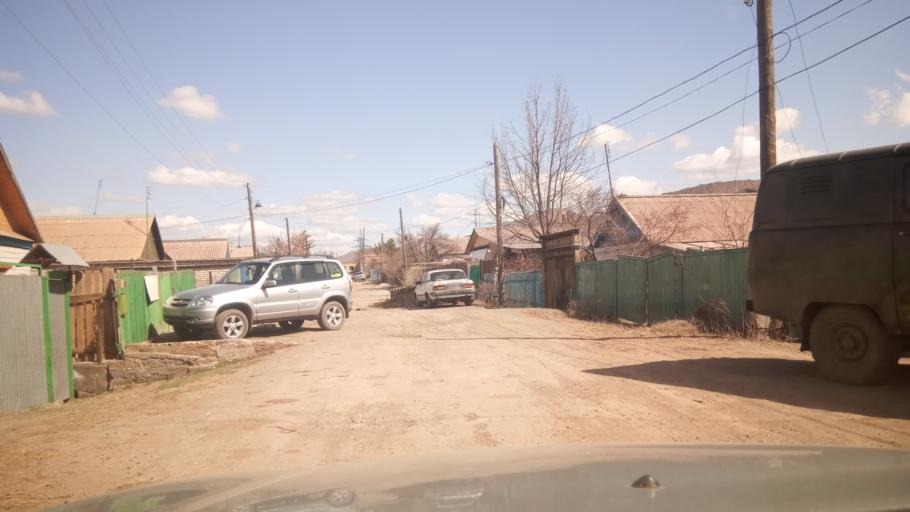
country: RU
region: Orenburg
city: Novotroitsk
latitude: 51.2084
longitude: 58.3166
